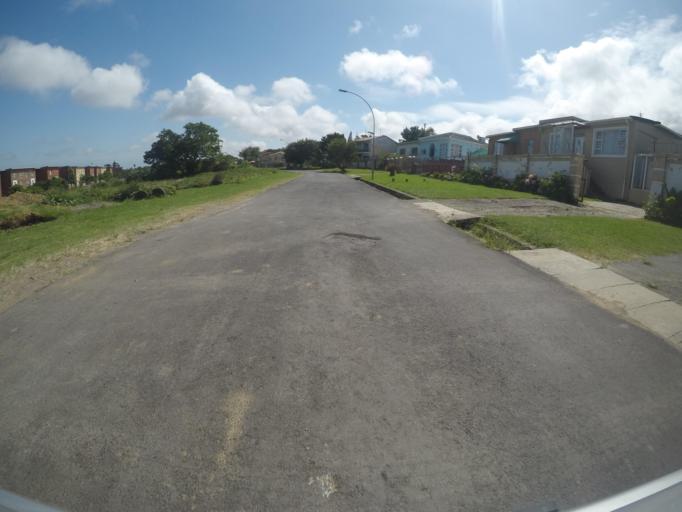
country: ZA
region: Eastern Cape
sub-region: Buffalo City Metropolitan Municipality
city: East London
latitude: -32.9968
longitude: 27.8954
